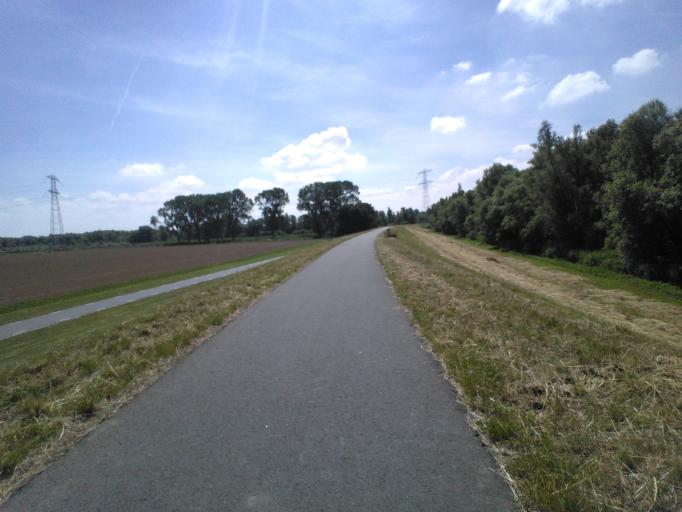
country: NL
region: North Brabant
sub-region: Gemeente Geertruidenberg
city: Geertruidenberg
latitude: 51.7338
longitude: 4.8583
